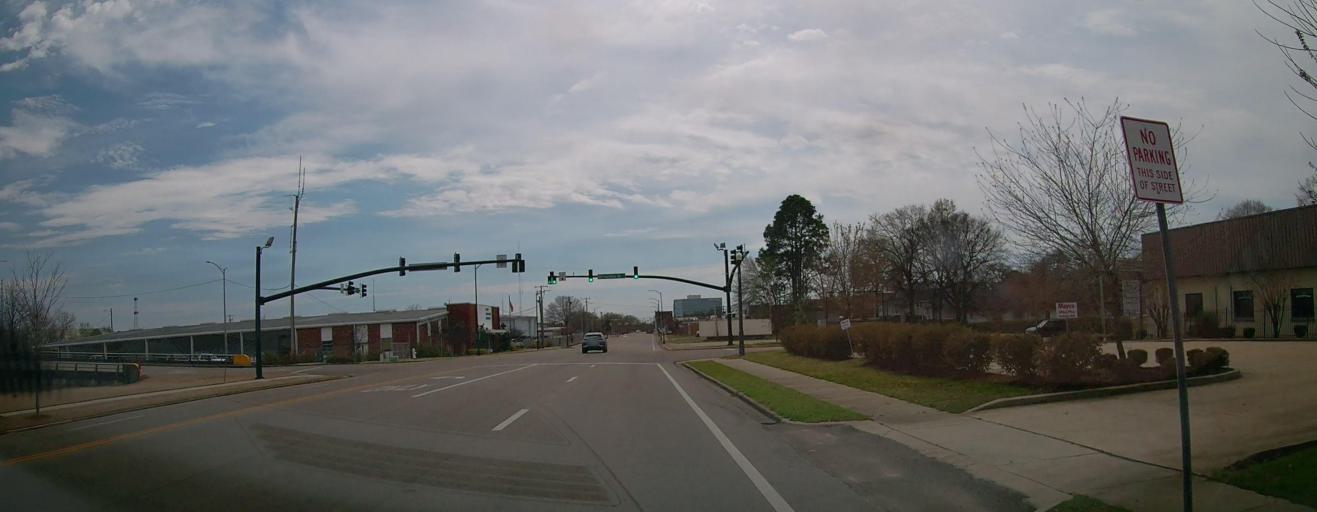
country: US
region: Mississippi
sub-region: Lee County
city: Tupelo
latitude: 34.2623
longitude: -88.7036
